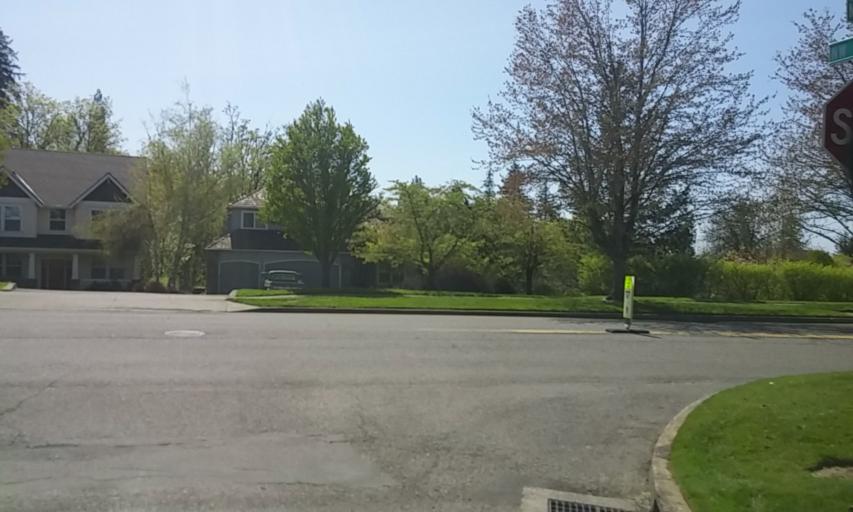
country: US
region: Oregon
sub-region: Washington County
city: West Haven
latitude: 45.5322
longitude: -122.7649
